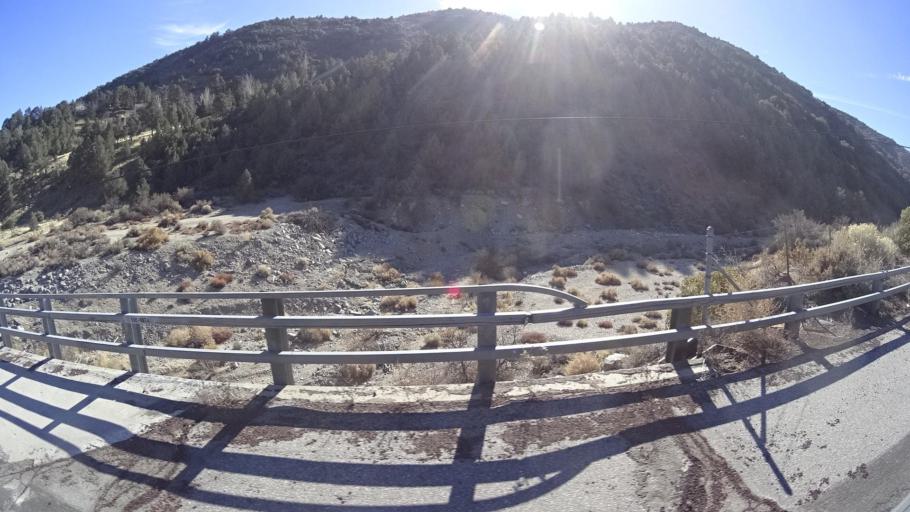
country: US
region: California
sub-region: Kern County
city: Frazier Park
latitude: 34.8201
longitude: -118.9576
